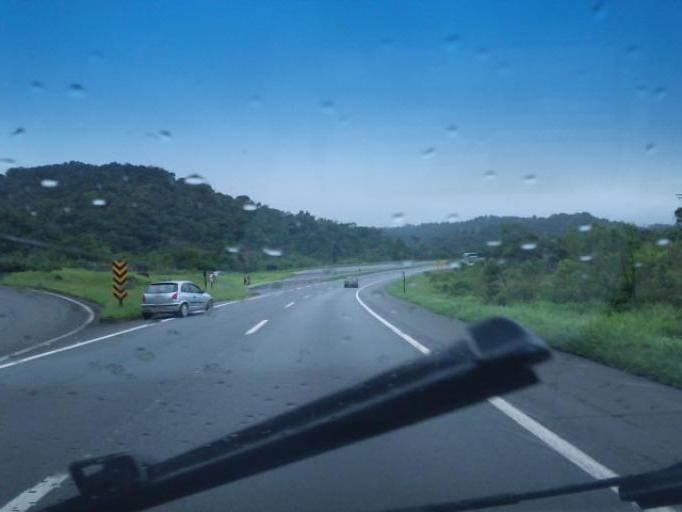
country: BR
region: Sao Paulo
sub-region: Cajati
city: Cajati
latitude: -24.9612
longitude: -48.4190
